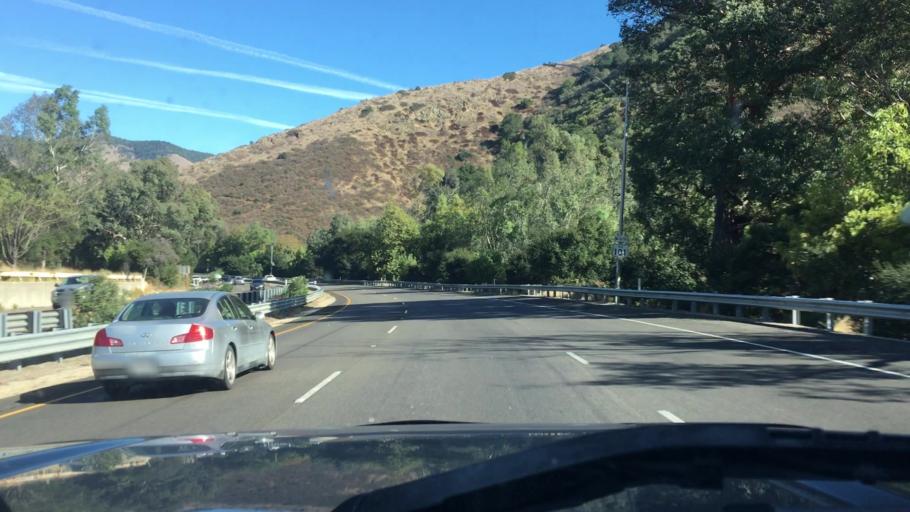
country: US
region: California
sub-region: San Luis Obispo County
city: San Luis Obispo
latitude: 35.2917
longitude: -120.6470
